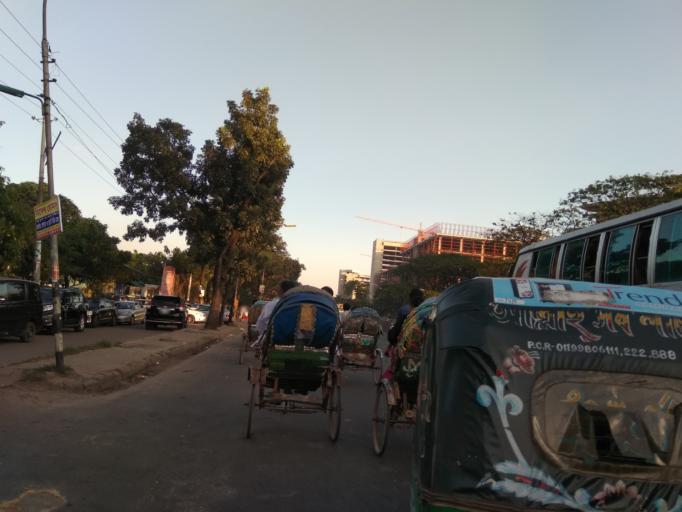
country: BD
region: Dhaka
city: Tungi
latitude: 23.8548
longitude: 90.4051
